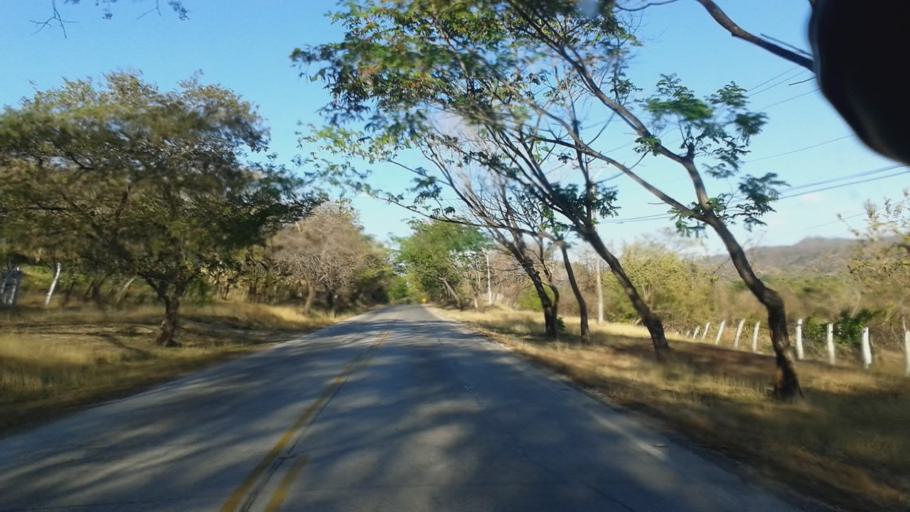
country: CR
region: Guanacaste
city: Nandayure
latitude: 10.2256
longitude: -85.1773
